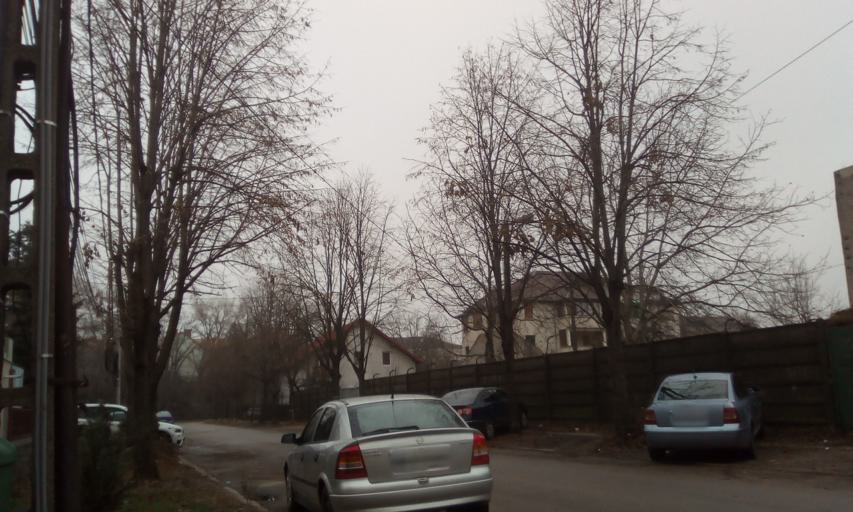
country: RO
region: Timis
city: Timisoara
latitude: 45.7521
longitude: 21.2435
